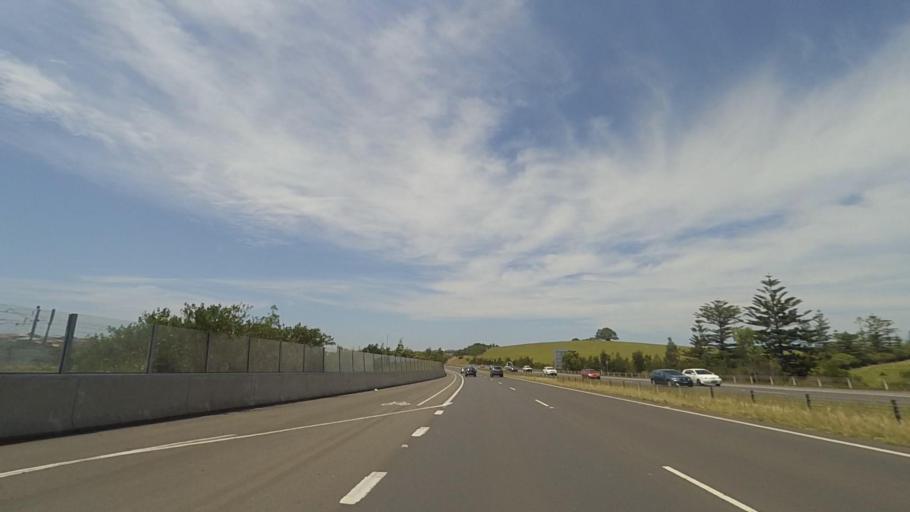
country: AU
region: New South Wales
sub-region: Shellharbour
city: Croom
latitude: -34.5817
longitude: 150.8375
